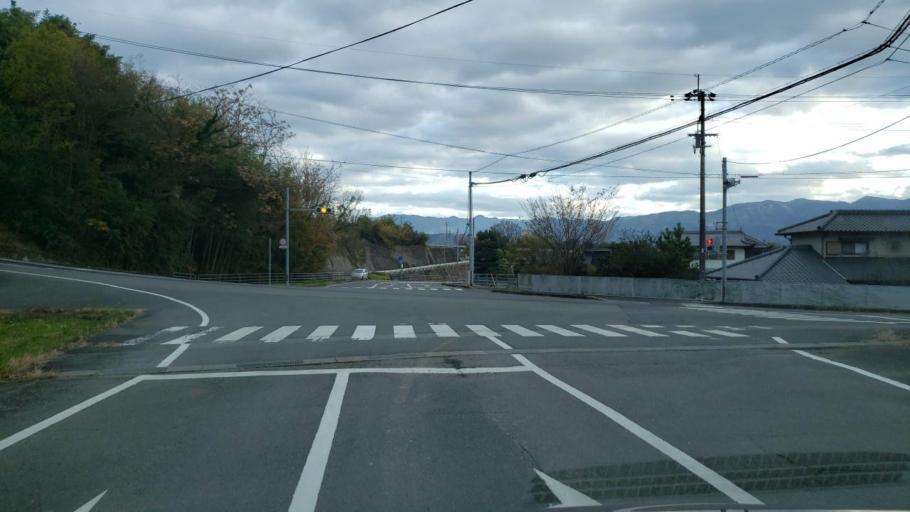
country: JP
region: Tokushima
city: Wakimachi
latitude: 34.1014
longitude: 134.2257
